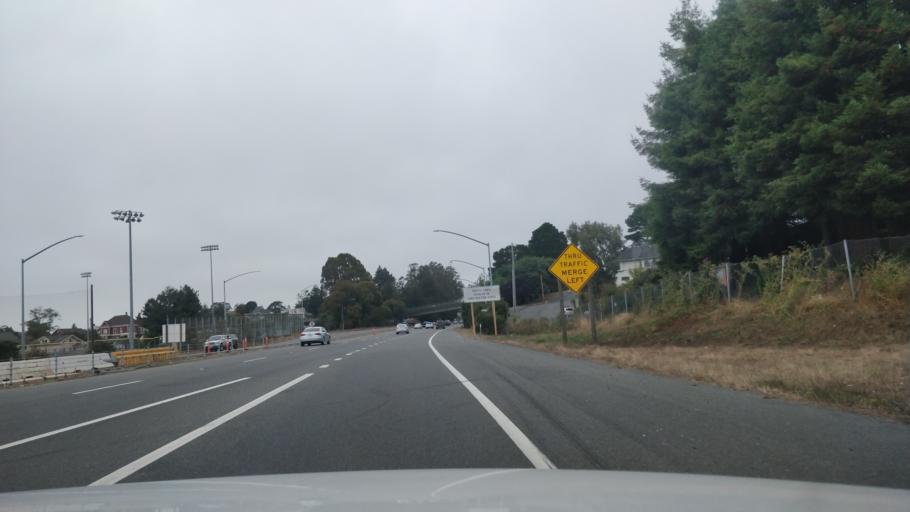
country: US
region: California
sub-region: Humboldt County
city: Arcata
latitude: 40.8664
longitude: -124.0829
